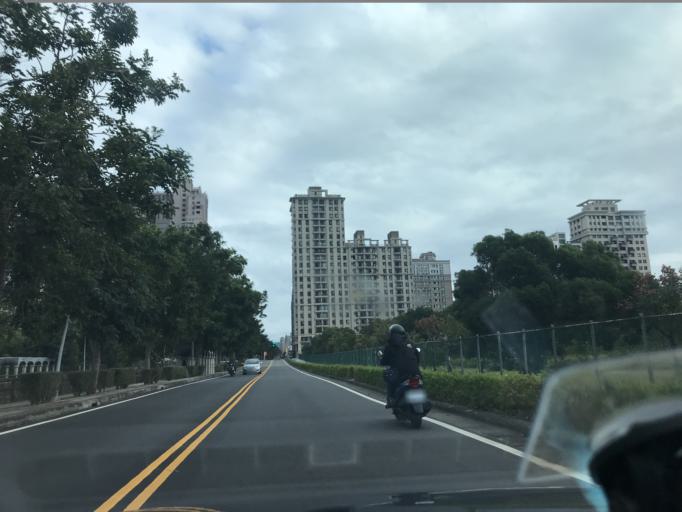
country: TW
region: Taiwan
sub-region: Hsinchu
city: Zhubei
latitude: 24.8274
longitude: 121.0226
